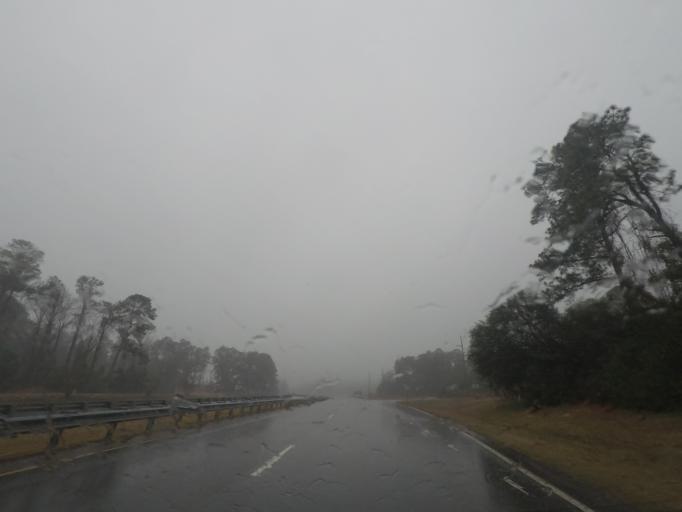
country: US
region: North Carolina
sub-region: Moore County
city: Southern Pines
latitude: 35.1752
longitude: -79.4026
